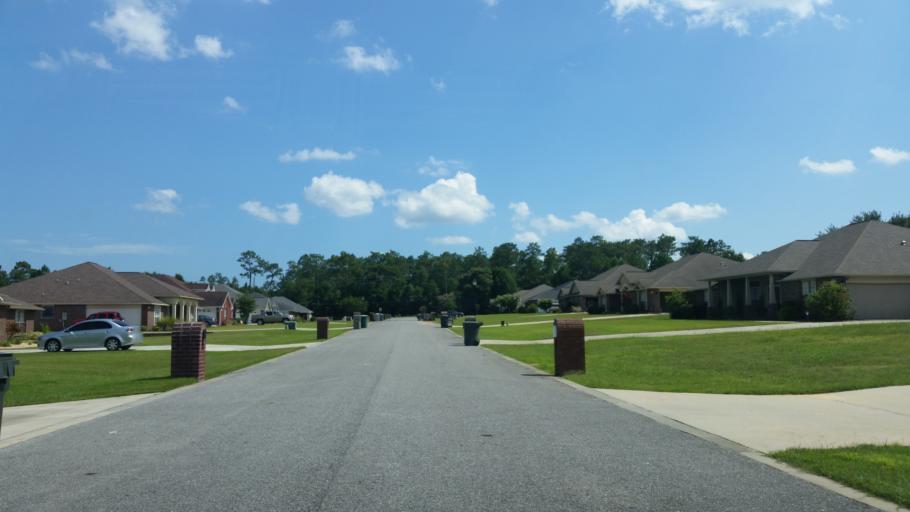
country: US
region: Florida
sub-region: Escambia County
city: Cantonment
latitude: 30.5524
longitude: -87.3831
